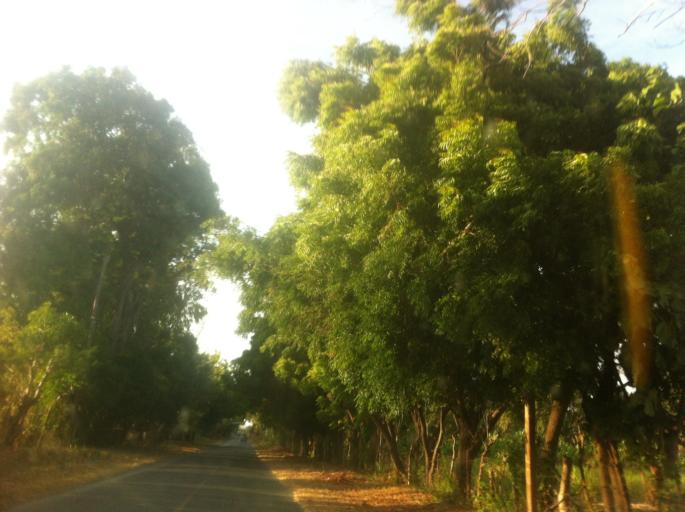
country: NI
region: Rivas
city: Buenos Aires
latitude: 11.4637
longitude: -85.8441
